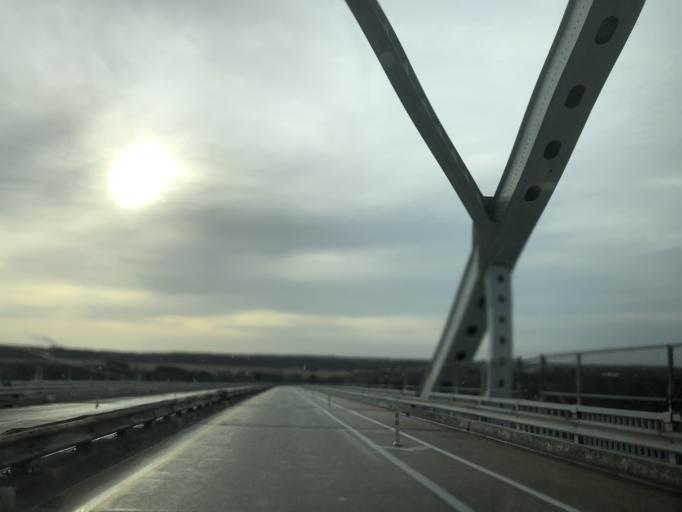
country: US
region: Delaware
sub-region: New Castle County
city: Delaware City
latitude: 39.5526
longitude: -75.6506
